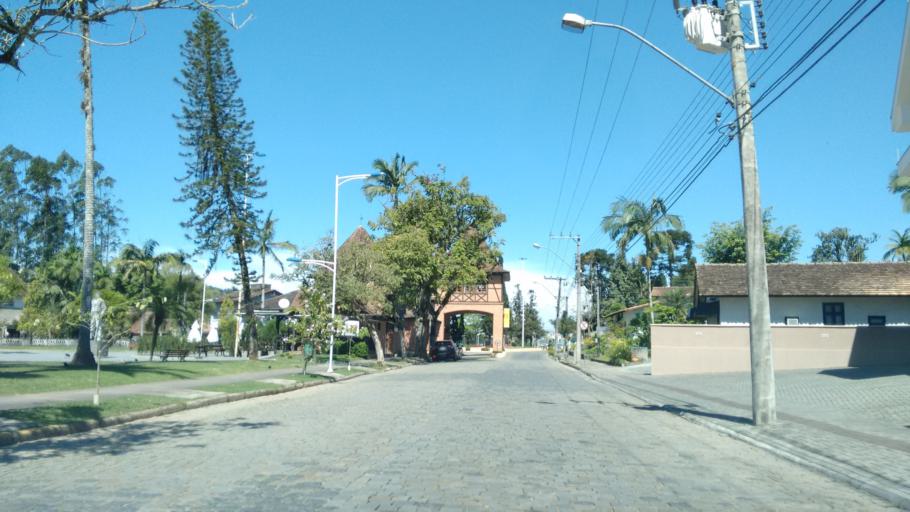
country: BR
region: Santa Catarina
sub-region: Pomerode
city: Pomerode
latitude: -26.7435
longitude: -49.1749
